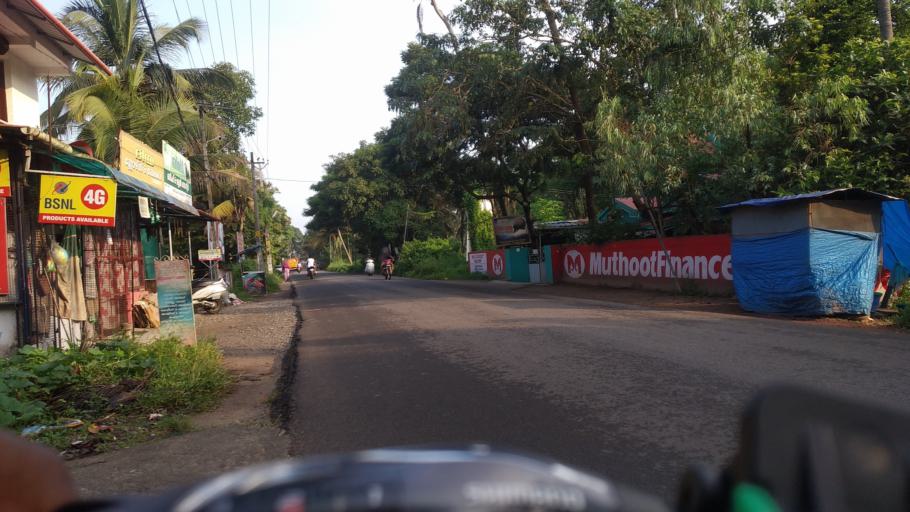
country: IN
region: Kerala
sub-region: Ernakulam
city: Elur
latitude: 10.0757
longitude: 76.2113
